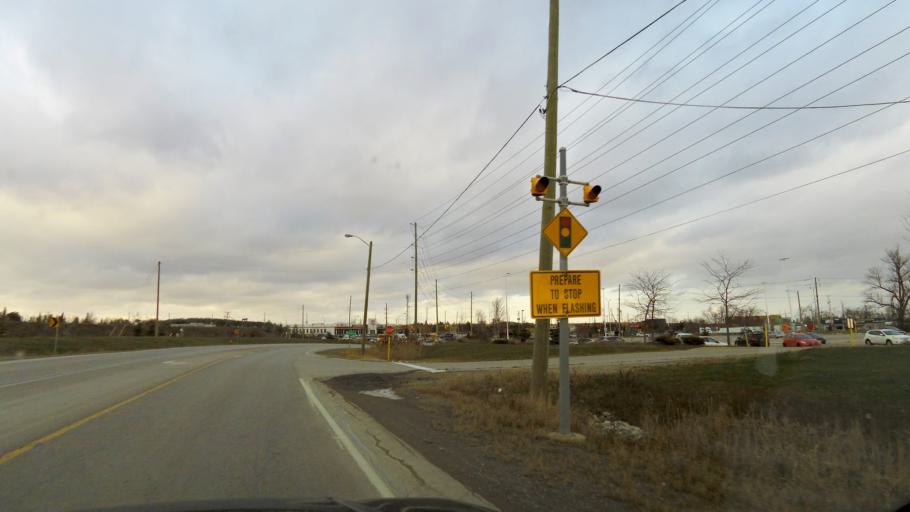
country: CA
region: Ontario
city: Brampton
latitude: 43.8471
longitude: -79.6973
